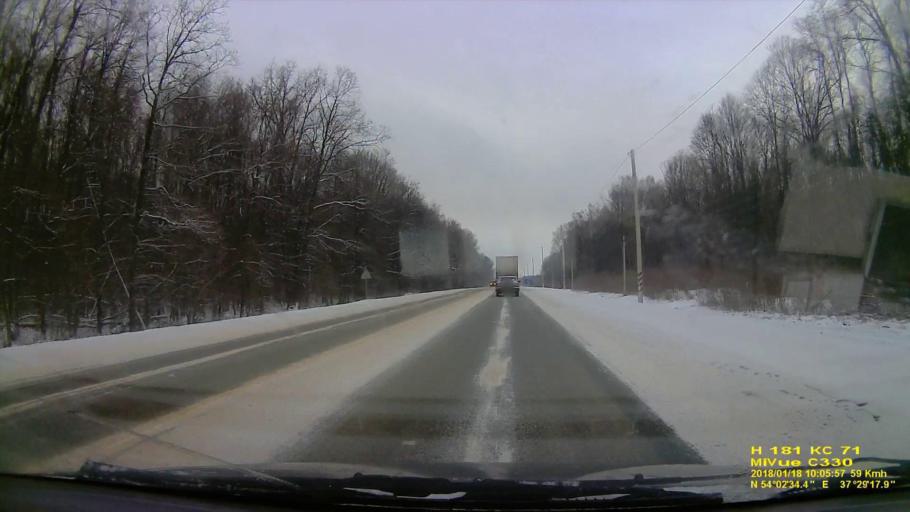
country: RU
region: Tula
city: Pervomayskiy
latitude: 54.0428
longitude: 37.4883
